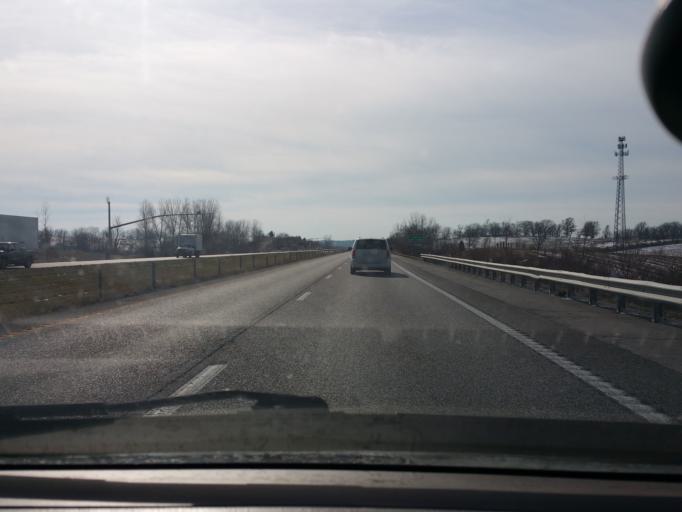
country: US
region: Missouri
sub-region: Clay County
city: Liberty
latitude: 39.2992
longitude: -94.4093
